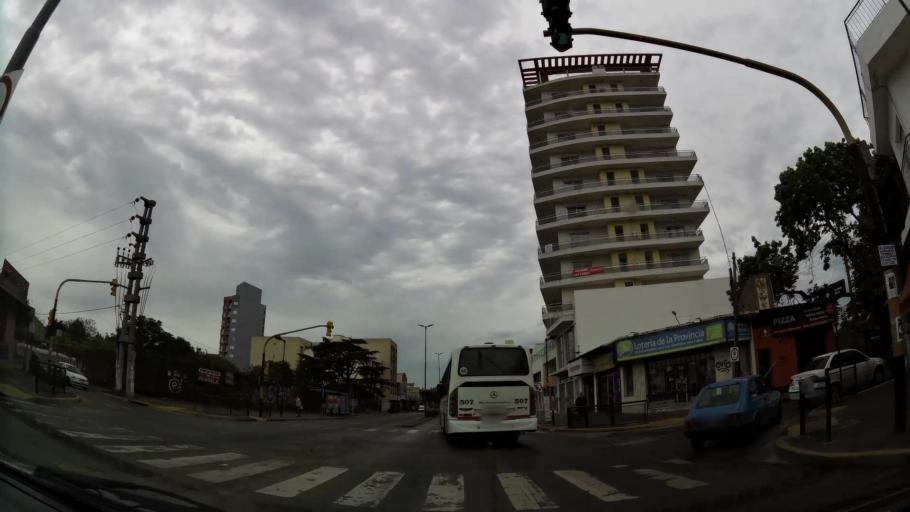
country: AR
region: Buenos Aires
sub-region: Partido de Quilmes
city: Quilmes
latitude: -34.7559
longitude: -58.2091
